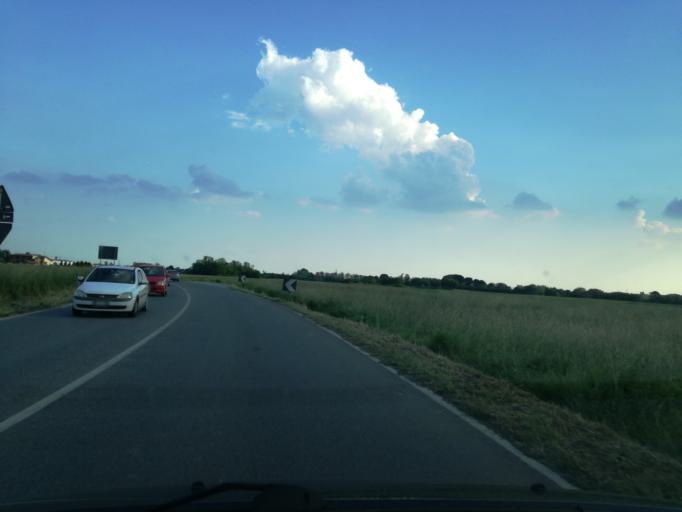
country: IT
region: Lombardy
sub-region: Provincia di Monza e Brianza
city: Cornate d'Adda
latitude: 45.6322
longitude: 9.4609
